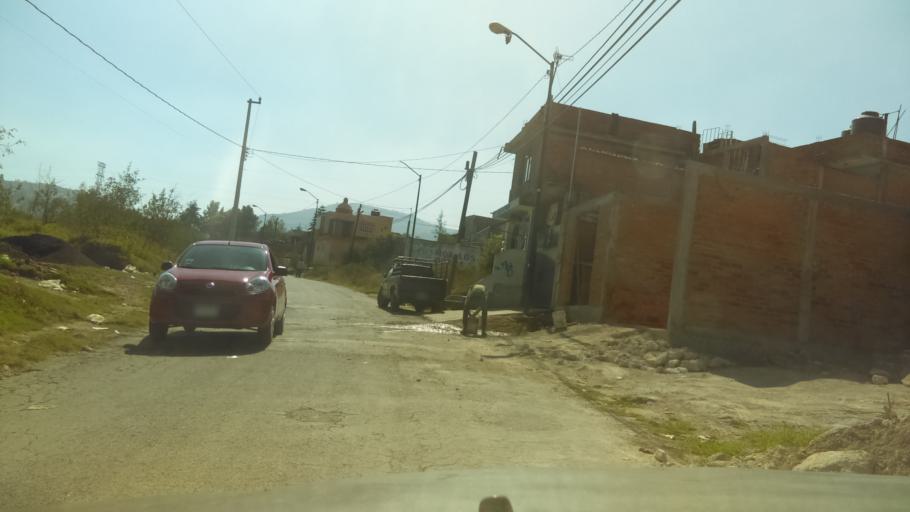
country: MX
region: Michoacan
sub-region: Morelia
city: Montana Monarca (Punta Altozano)
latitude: 19.6593
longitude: -101.1828
